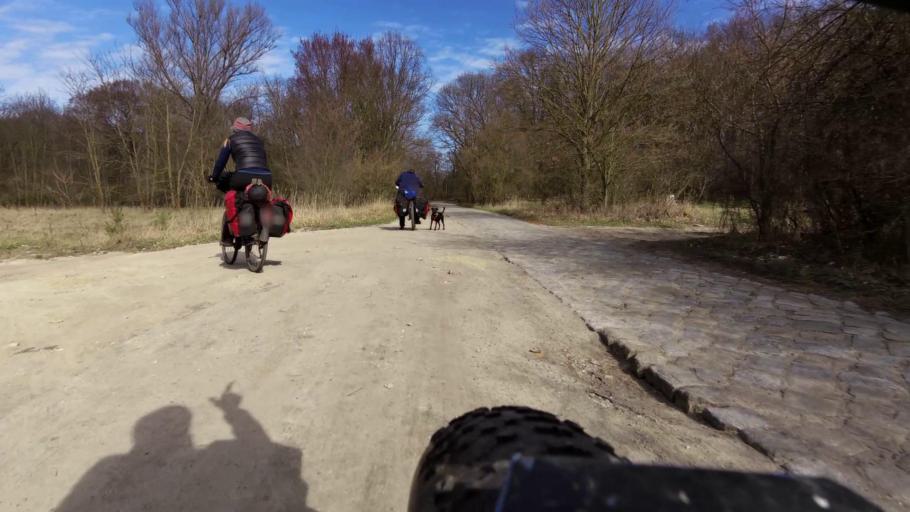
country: PL
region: Lubusz
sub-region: Powiat slubicki
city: Slubice
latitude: 52.3220
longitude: 14.5822
